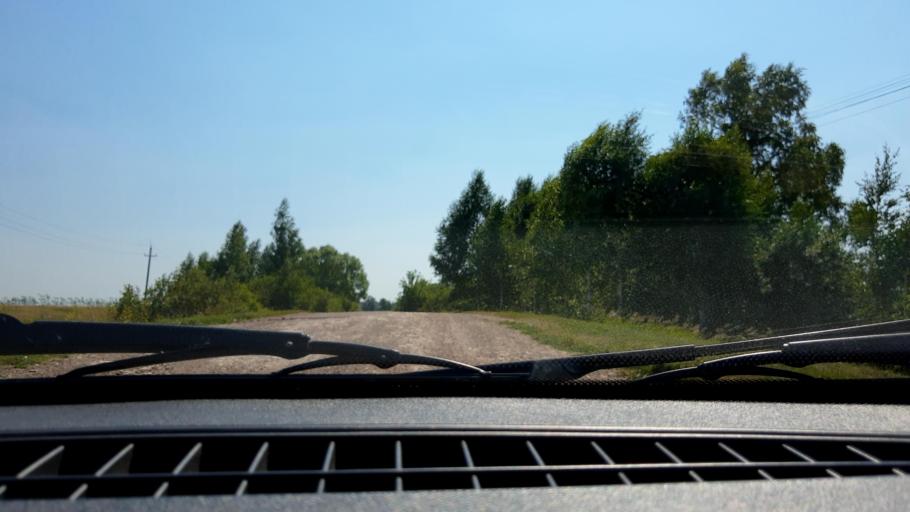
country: RU
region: Bashkortostan
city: Kushnarenkovo
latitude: 55.0671
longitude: 55.1643
